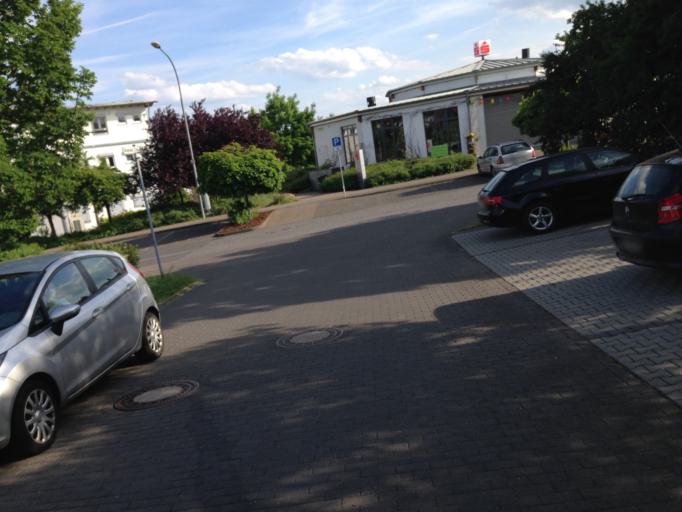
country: DE
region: Hesse
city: Staufenberg
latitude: 50.6586
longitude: 8.7353
